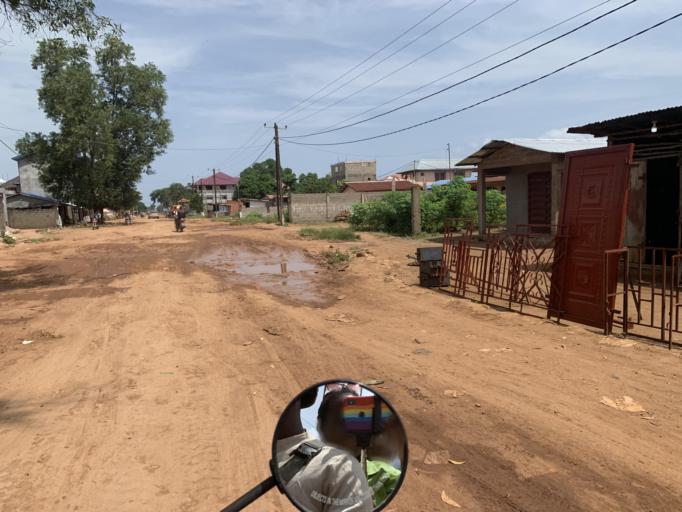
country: SL
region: Western Area
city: Hastings
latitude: 8.3996
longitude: -13.1395
